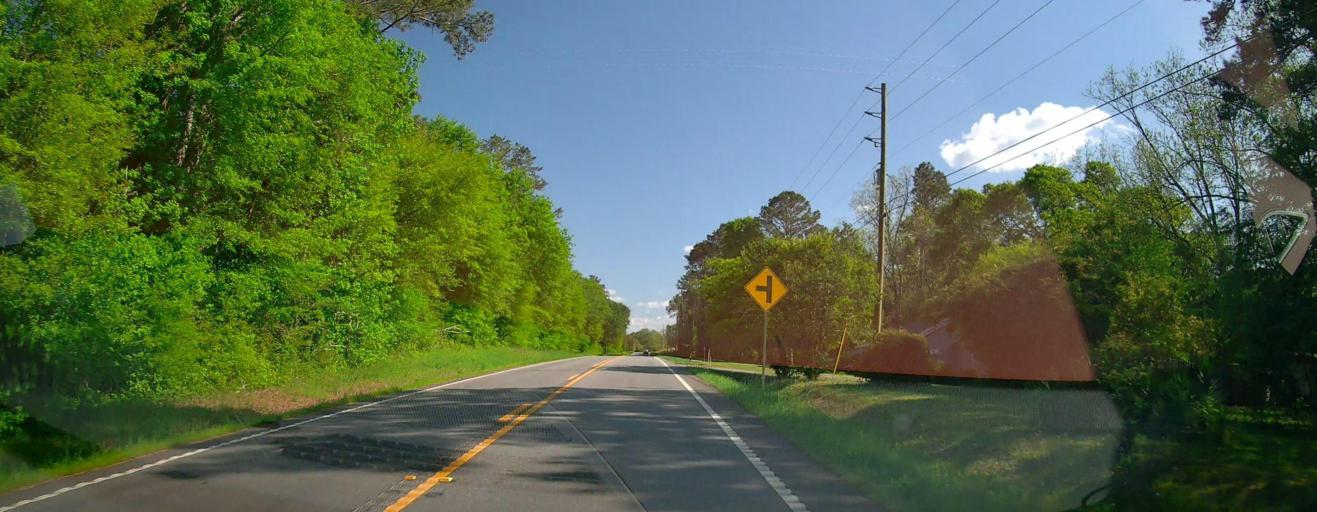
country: US
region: Georgia
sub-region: Morgan County
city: Madison
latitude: 33.6186
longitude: -83.4819
